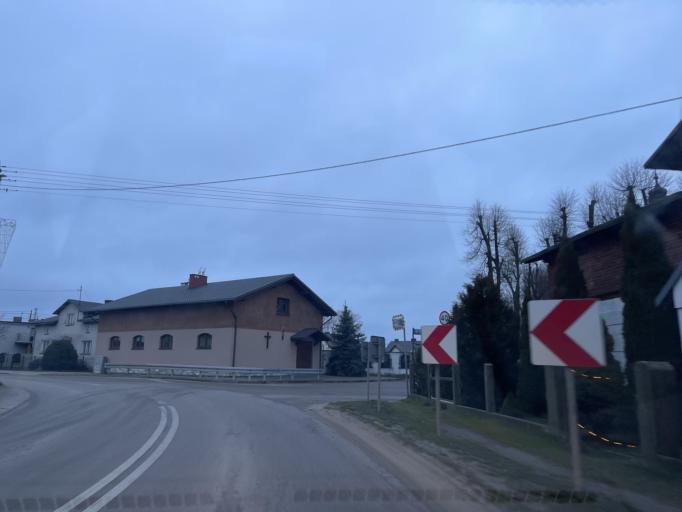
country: PL
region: Pomeranian Voivodeship
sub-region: Powiat wejherowski
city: Szemud
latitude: 54.4147
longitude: 18.2022
